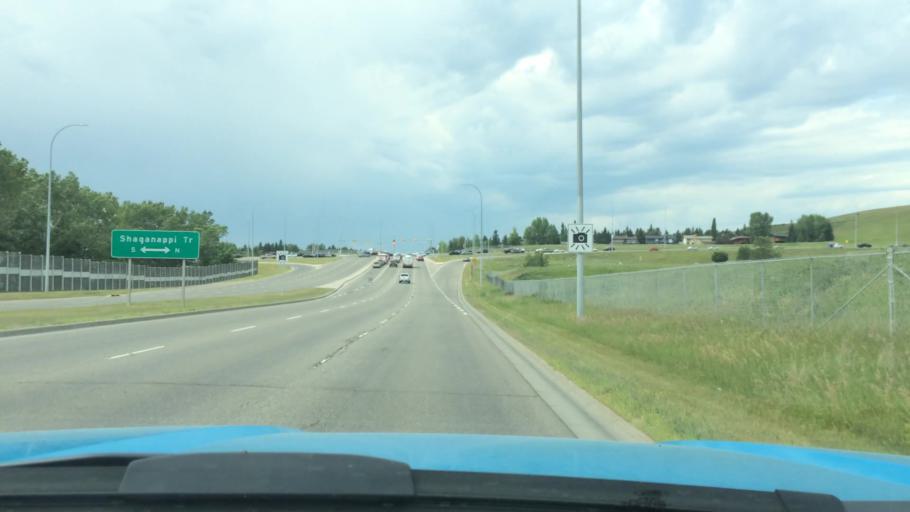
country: CA
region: Alberta
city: Calgary
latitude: 51.1075
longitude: -114.1359
